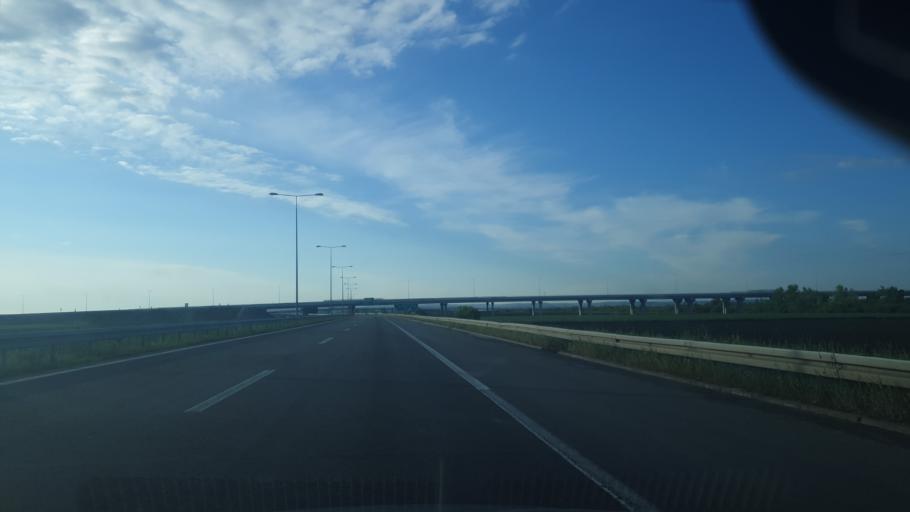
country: RS
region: Central Serbia
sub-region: Belgrade
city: Surcin
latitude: 44.7759
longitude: 20.2695
